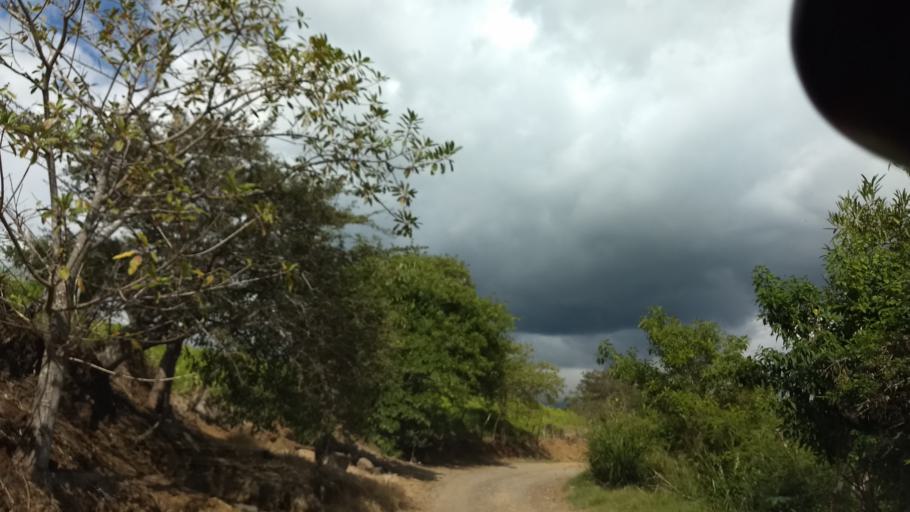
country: MX
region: Colima
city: Suchitlan
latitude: 19.4563
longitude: -103.7685
